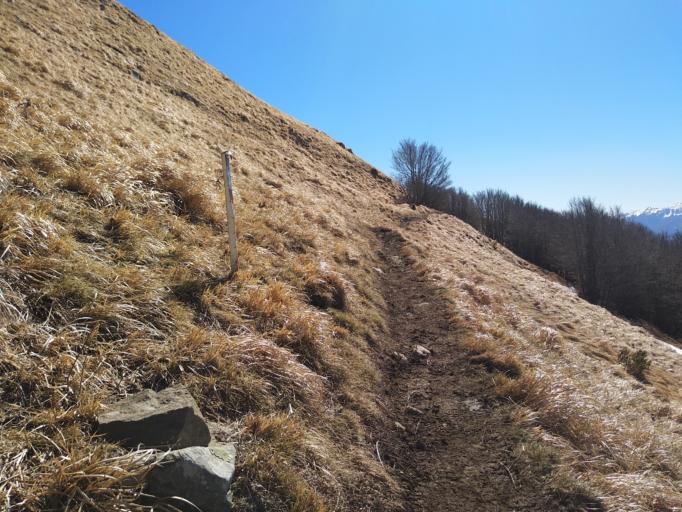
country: IT
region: Emilia-Romagna
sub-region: Provincia di Reggio Emilia
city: Collagna
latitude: 44.3738
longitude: 10.2848
